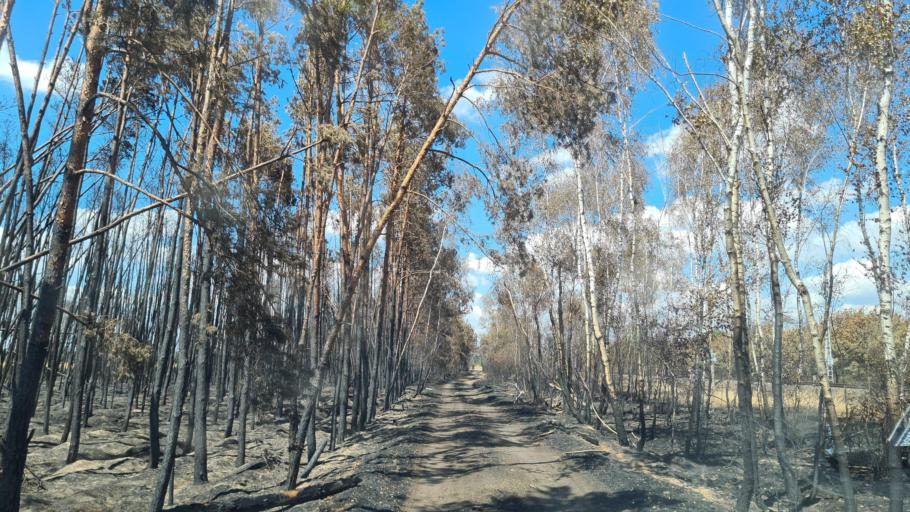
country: DE
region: Brandenburg
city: Muhlberg
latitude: 51.4276
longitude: 13.3050
